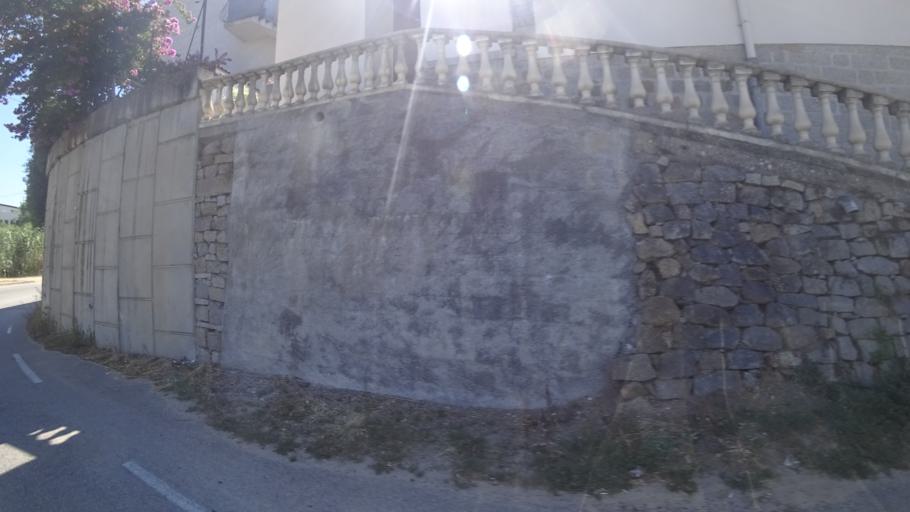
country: FR
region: Corsica
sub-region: Departement de la Corse-du-Sud
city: Ajaccio
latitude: 41.9392
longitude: 8.7382
